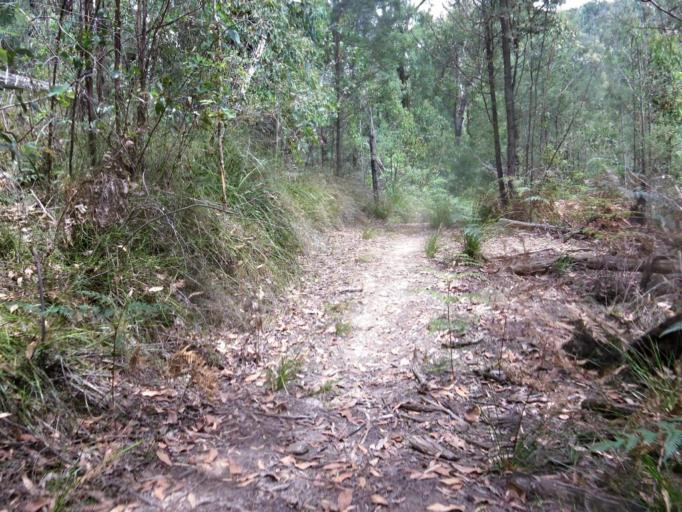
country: AU
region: Victoria
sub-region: Yarra Ranges
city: Healesville
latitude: -37.4464
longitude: 145.5849
